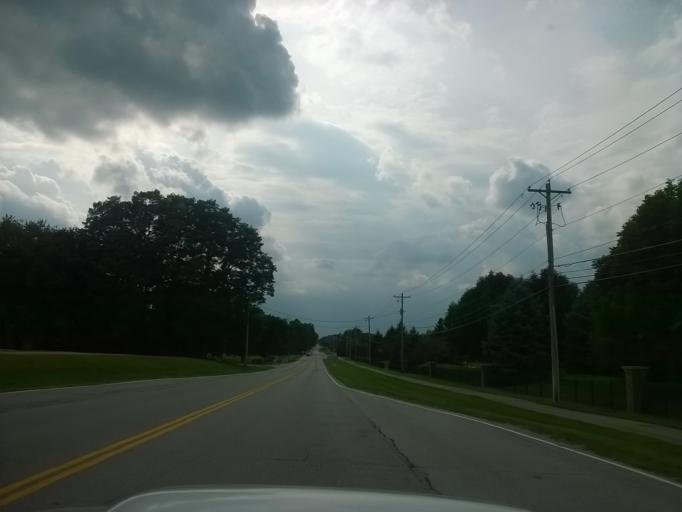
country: US
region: Indiana
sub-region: Hamilton County
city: Carmel
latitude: 39.9785
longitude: -86.0763
